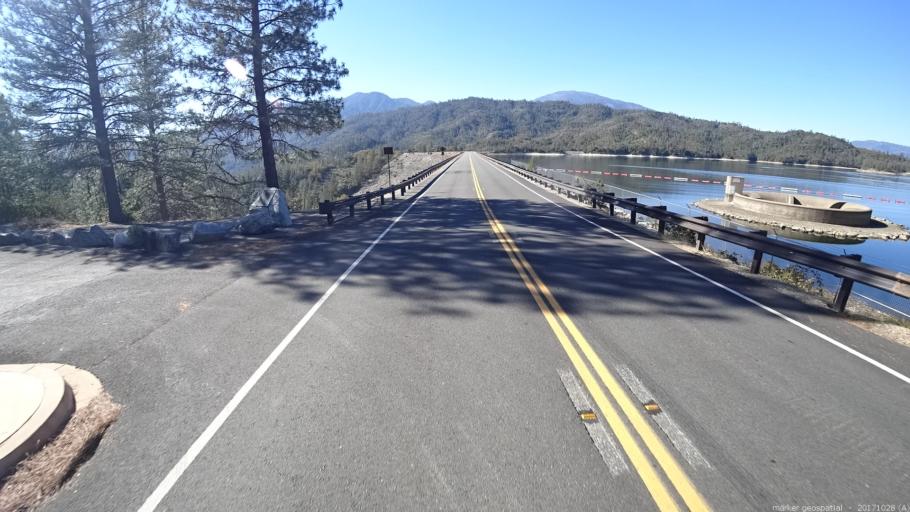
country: US
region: California
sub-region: Shasta County
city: Shasta
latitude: 40.6001
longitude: -122.5356
